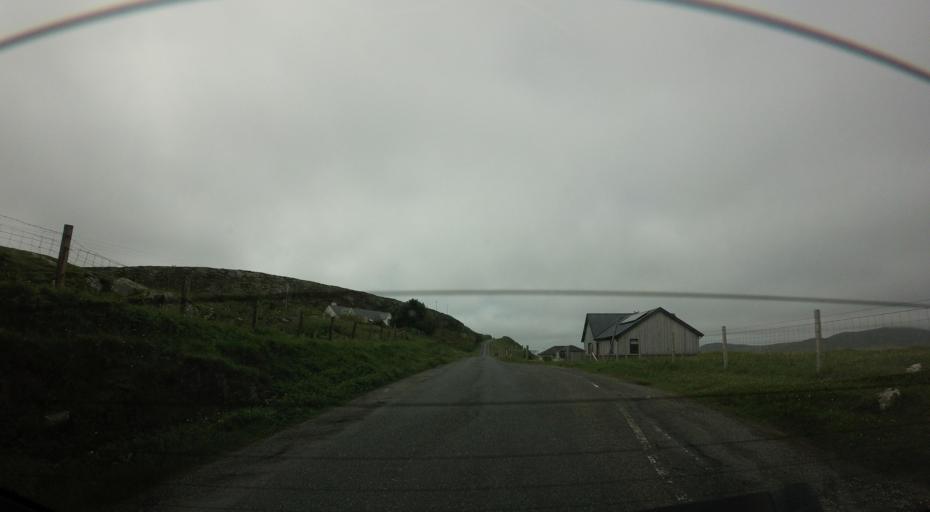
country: GB
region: Scotland
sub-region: Eilean Siar
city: Harris
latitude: 57.8671
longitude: -6.9581
